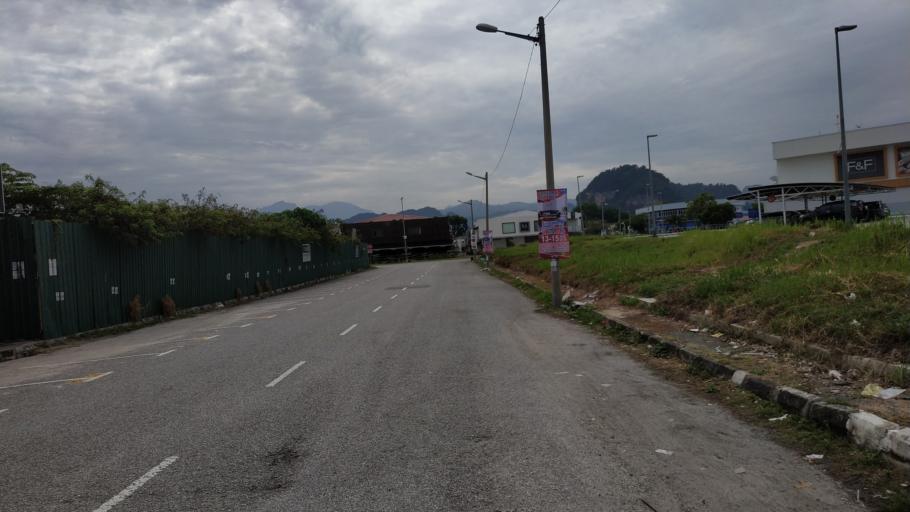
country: MY
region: Perak
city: Ipoh
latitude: 4.6176
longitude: 101.1178
